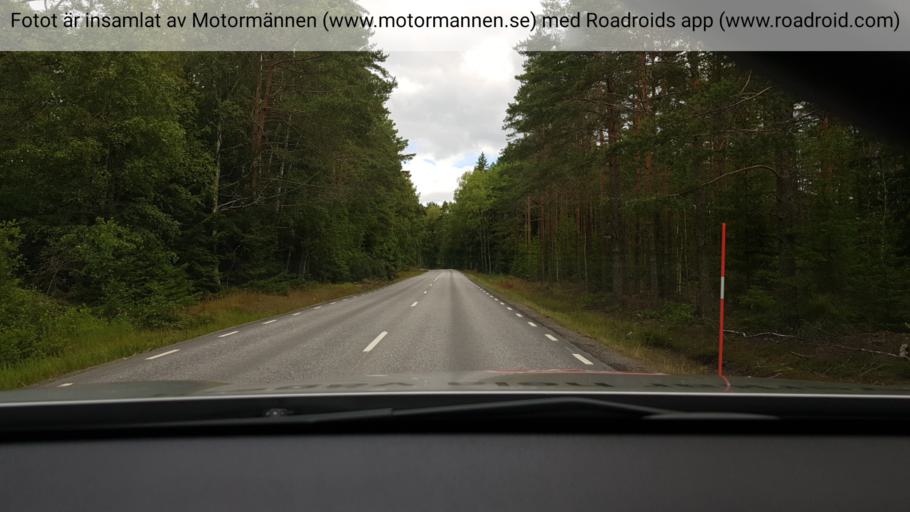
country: SE
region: Stockholm
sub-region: Haninge Kommun
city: Haninge
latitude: 59.1601
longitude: 18.1812
